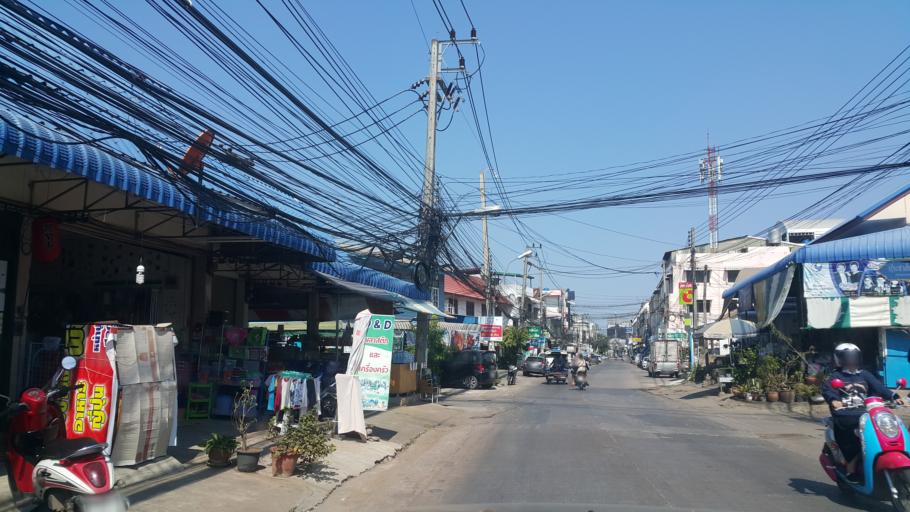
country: TH
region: Changwat Udon Thani
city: Udon Thani
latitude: 17.3927
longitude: 102.8095
